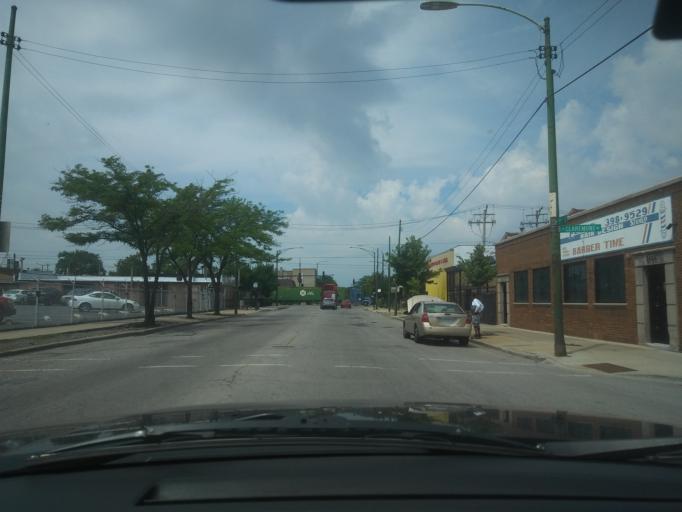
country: US
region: Illinois
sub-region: Cook County
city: Evergreen Park
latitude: 41.7865
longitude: -87.6824
